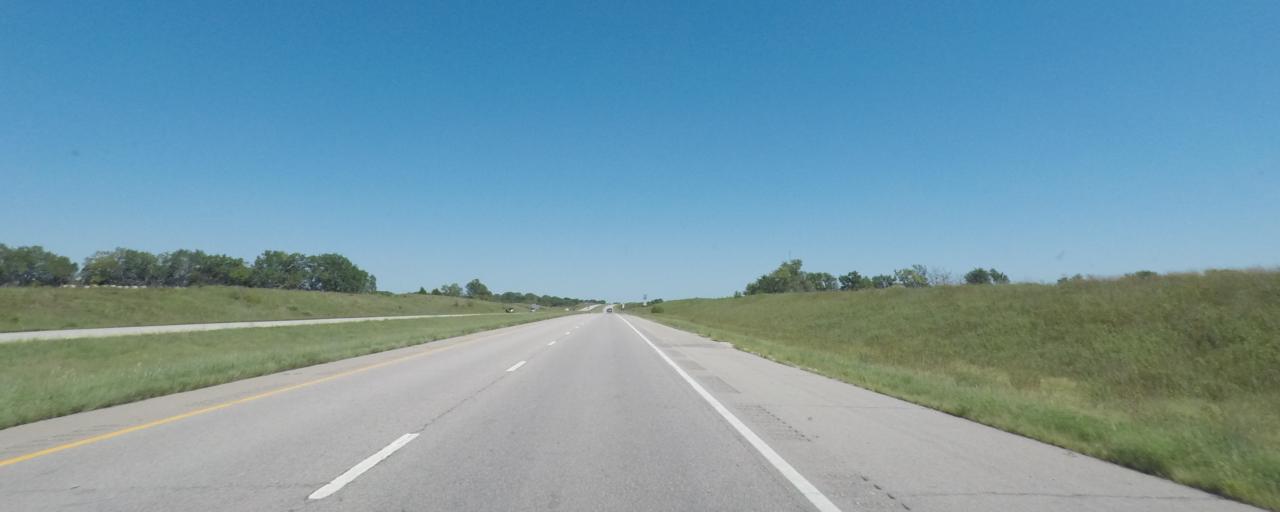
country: US
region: Kansas
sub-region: Lyon County
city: Emporia
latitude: 38.4103
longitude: -96.0358
